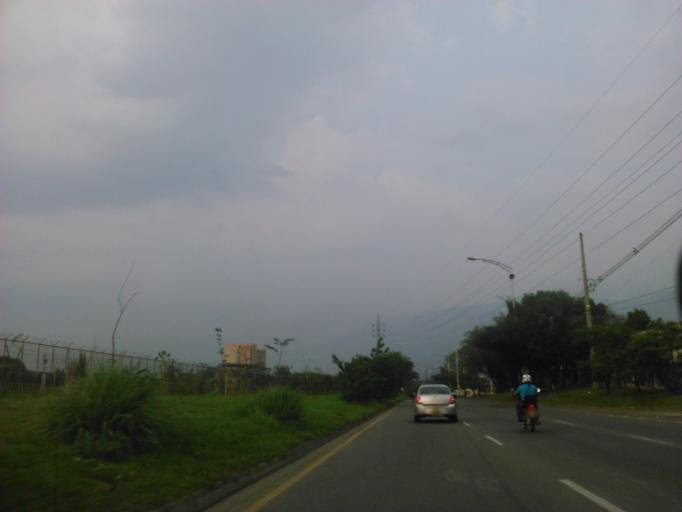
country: CO
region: Antioquia
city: Sabaneta
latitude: 6.1605
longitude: -75.6109
